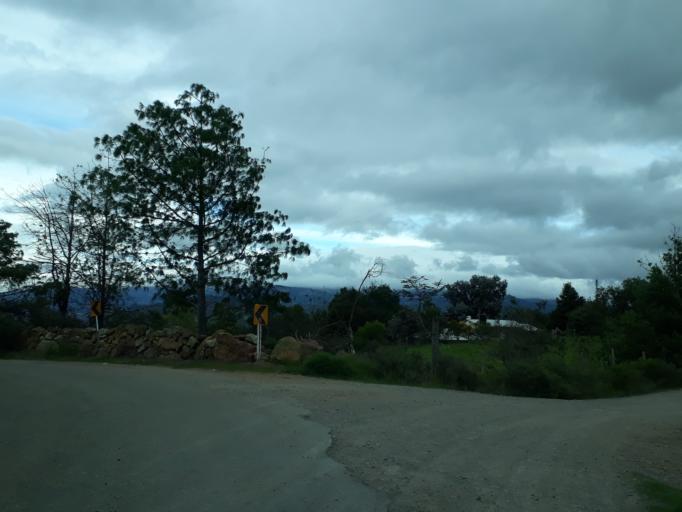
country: CO
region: Cundinamarca
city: Susa
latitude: 5.3961
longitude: -73.7821
